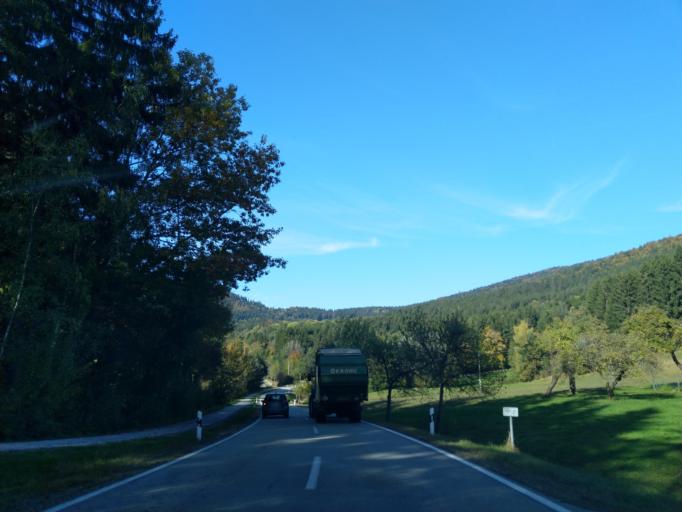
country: DE
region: Bavaria
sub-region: Lower Bavaria
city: Bernried
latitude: 48.9179
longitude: 12.9230
